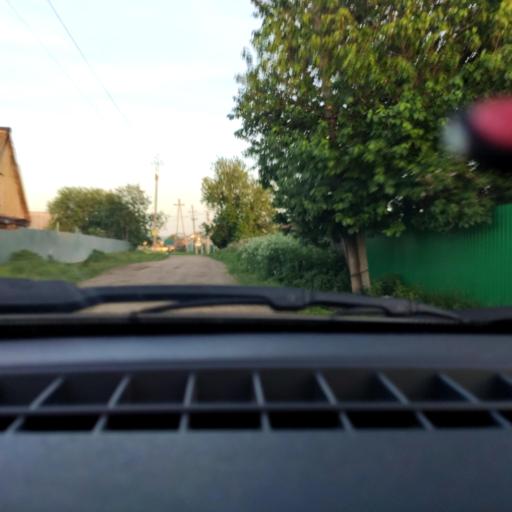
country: RU
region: Bashkortostan
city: Tolbazy
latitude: 54.2975
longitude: 55.8126
